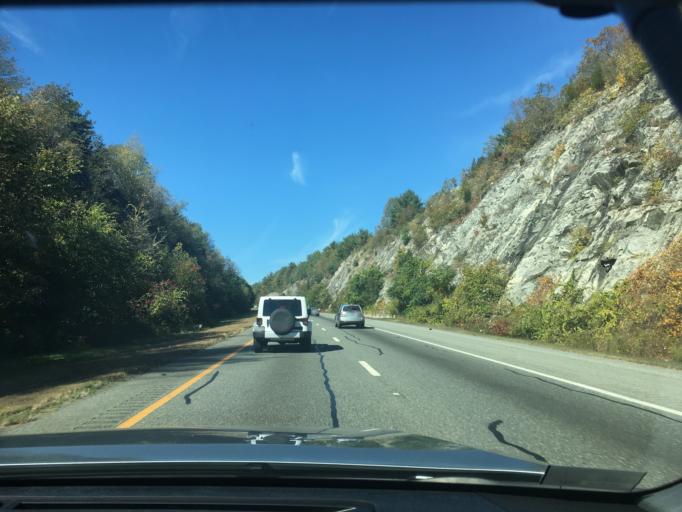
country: US
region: Rhode Island
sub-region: Providence County
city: Cranston
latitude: 41.7704
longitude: -71.4847
